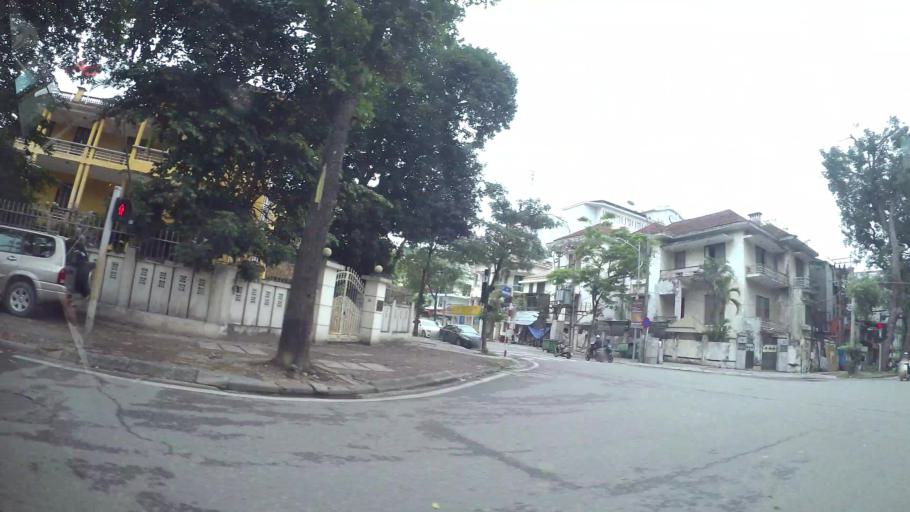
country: VN
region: Ha Noi
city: Hanoi
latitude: 21.0197
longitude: 105.8444
